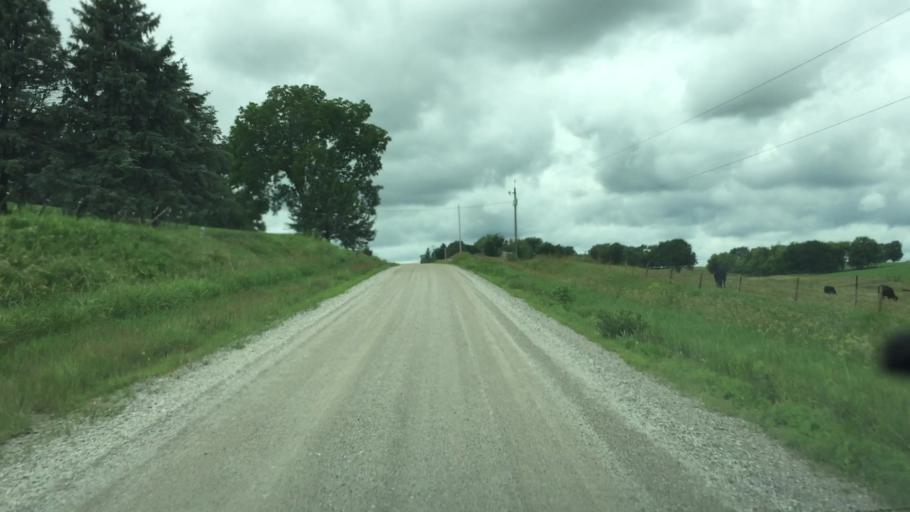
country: US
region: Iowa
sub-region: Jasper County
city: Prairie City
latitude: 41.6010
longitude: -93.1455
